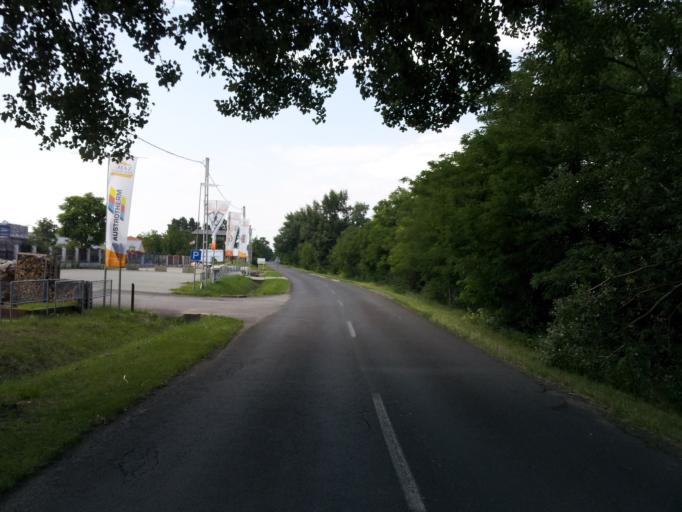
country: HU
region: Pest
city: Toekoel
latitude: 47.2953
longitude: 18.9802
